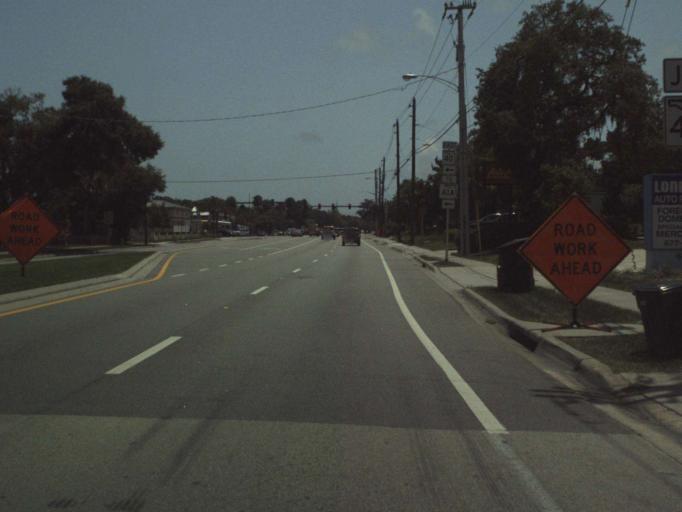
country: US
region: Florida
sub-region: Volusia County
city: Ormond Beach
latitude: 29.2848
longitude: -81.0632
